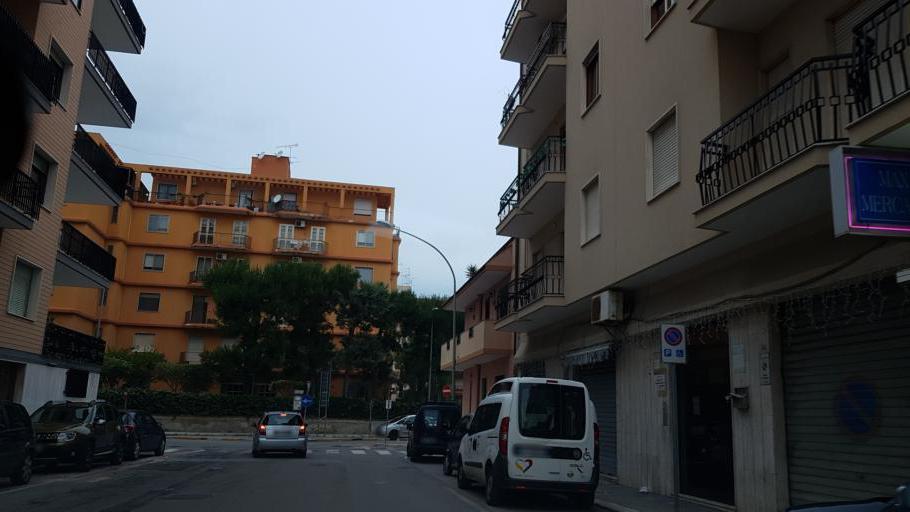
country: IT
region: Apulia
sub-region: Provincia di Brindisi
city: Brindisi
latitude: 40.6317
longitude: 17.9240
